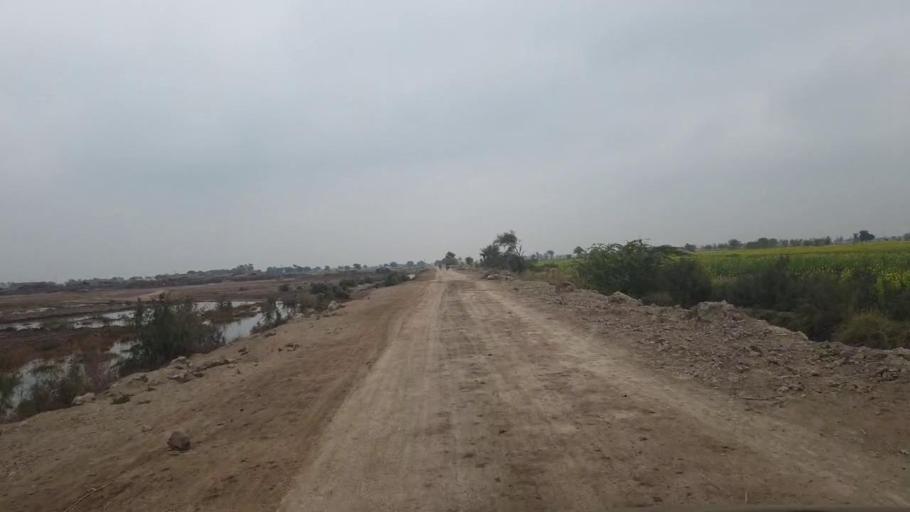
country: PK
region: Sindh
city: Shahdadpur
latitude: 25.9056
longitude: 68.7124
